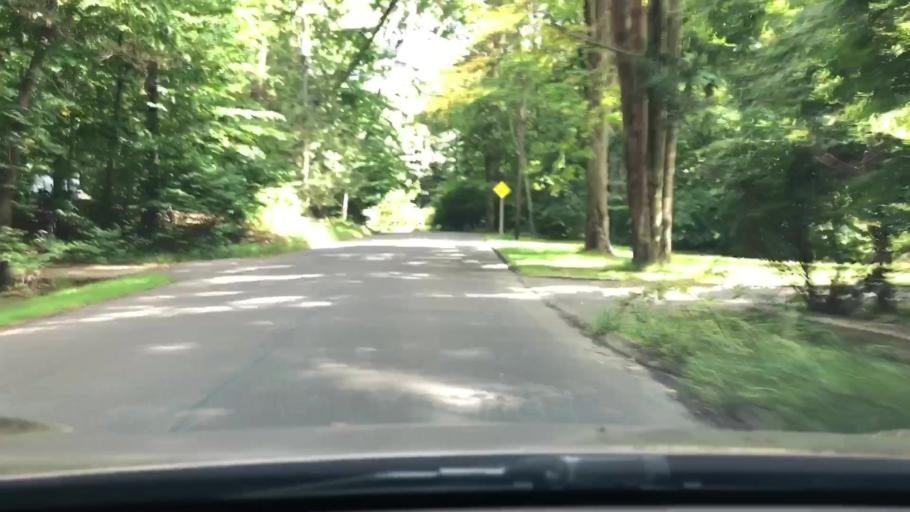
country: US
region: Connecticut
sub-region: Fairfield County
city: Darien
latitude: 41.1103
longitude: -73.4589
